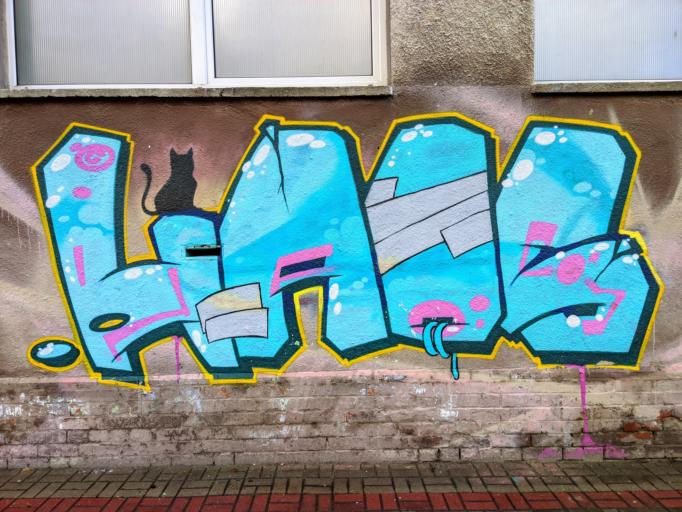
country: PL
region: Lubusz
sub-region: Powiat swiebodzinski
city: Swiebodzin
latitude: 52.2500
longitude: 15.5382
